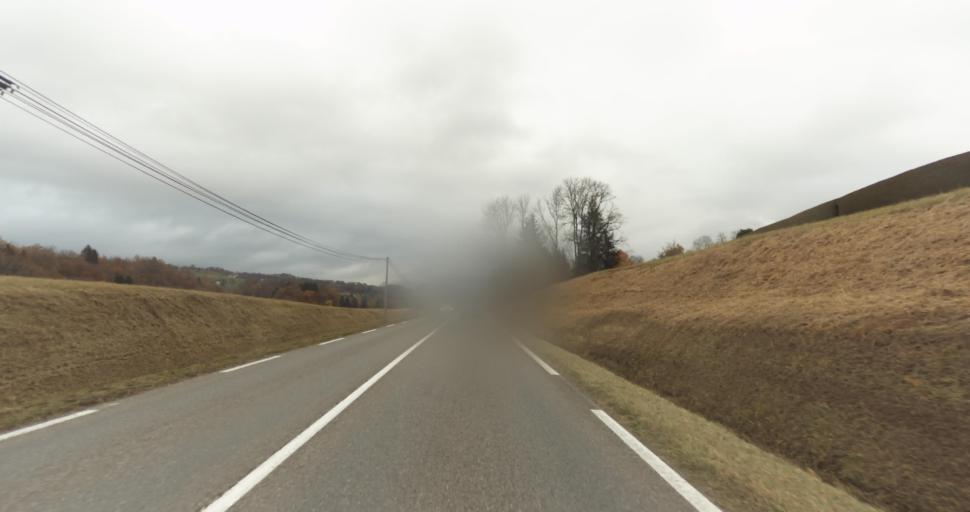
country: FR
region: Rhone-Alpes
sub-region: Departement de la Haute-Savoie
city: Saint-Martin-Bellevue
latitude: 45.9654
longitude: 6.1646
